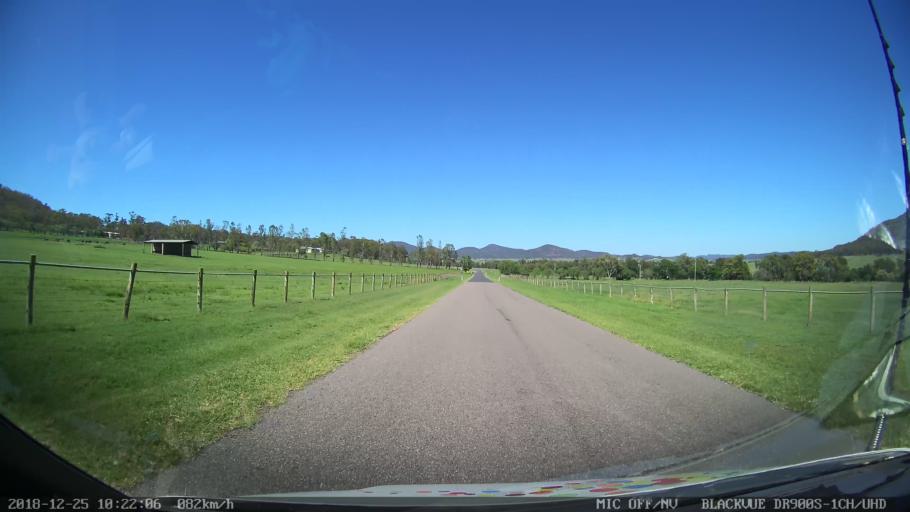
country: AU
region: New South Wales
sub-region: Muswellbrook
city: Denman
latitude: -32.3739
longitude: 150.5364
